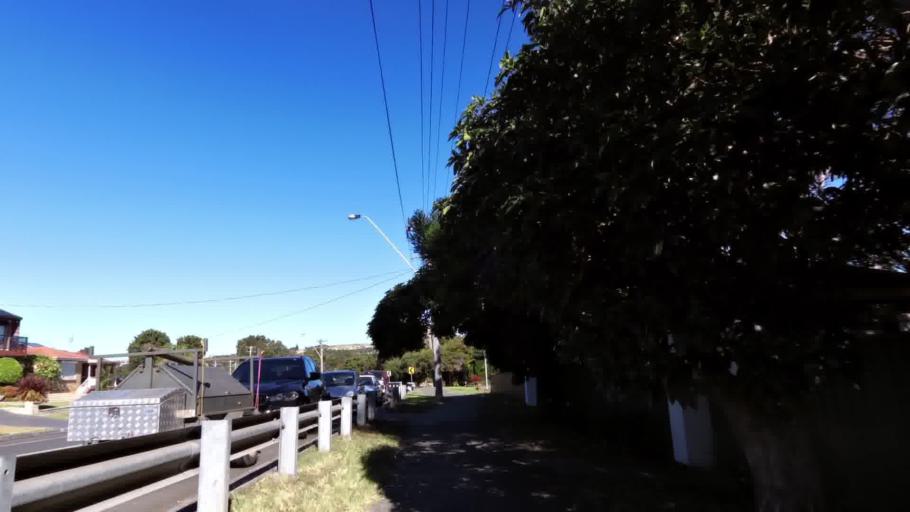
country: AU
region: New South Wales
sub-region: Shellharbour
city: Lake Illawarra
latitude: -34.5536
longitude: 150.8343
